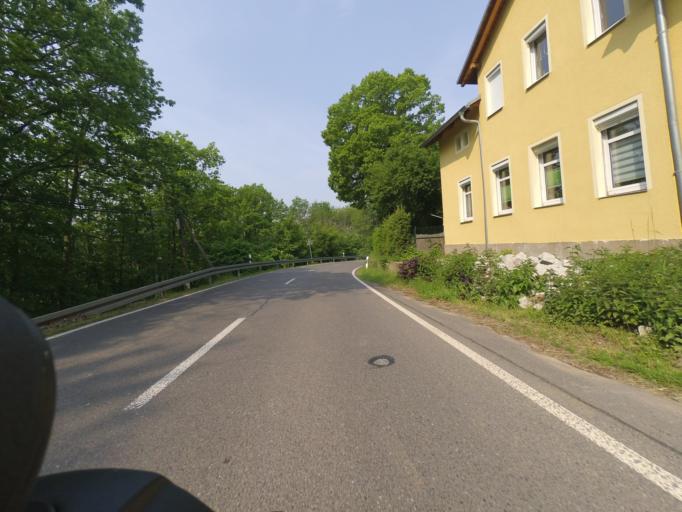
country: DE
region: Saxony
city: Rabenau
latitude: 50.9664
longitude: 13.6295
